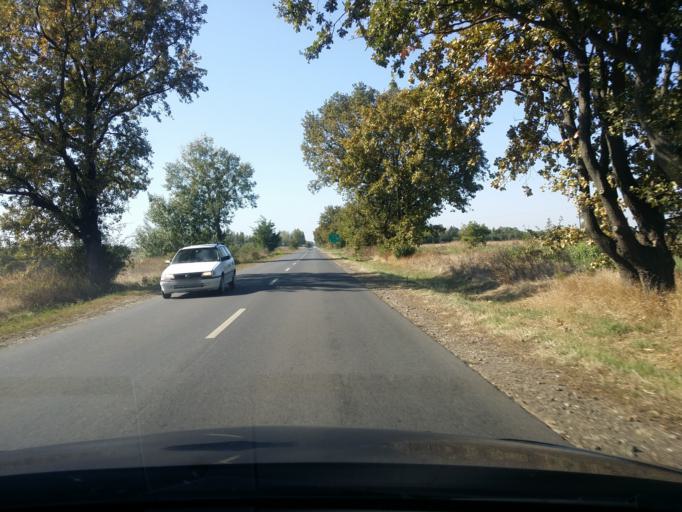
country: HU
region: Jasz-Nagykun-Szolnok
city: Ocsod
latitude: 46.9982
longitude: 20.4025
